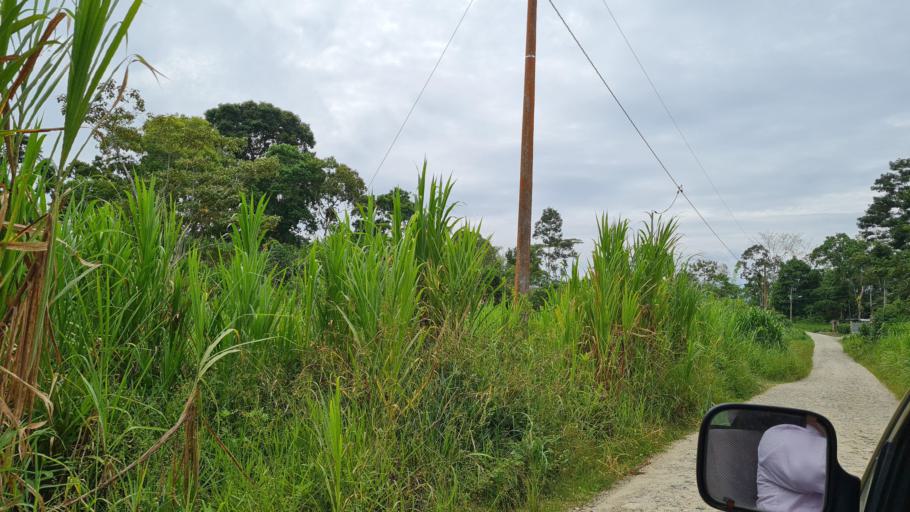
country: EC
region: Napo
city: Tena
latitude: -1.0018
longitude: -77.7649
